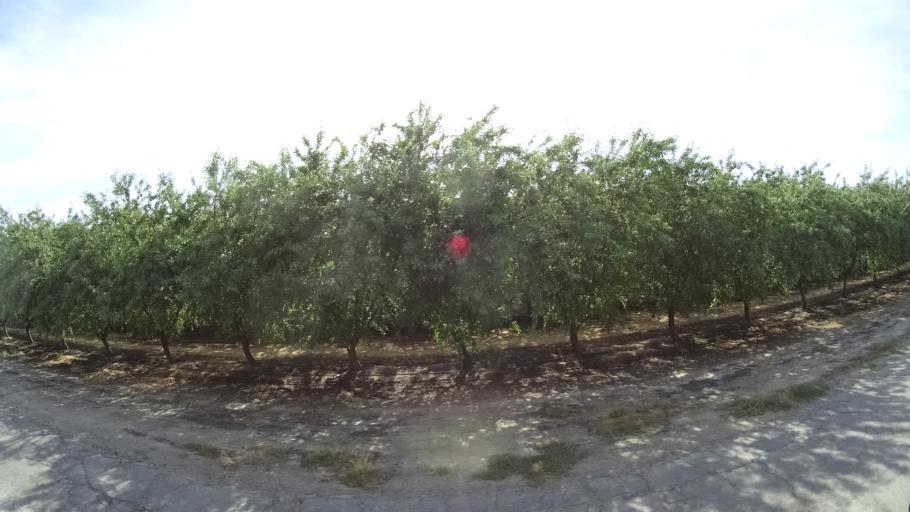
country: US
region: California
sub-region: Tulare County
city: Goshen
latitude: 36.3298
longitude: -119.4842
